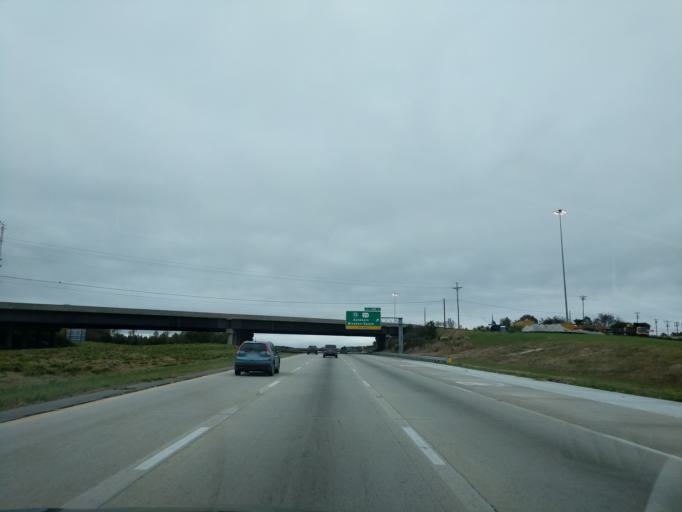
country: US
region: North Carolina
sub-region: Randolph County
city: Archdale
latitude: 35.9212
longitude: -79.9381
